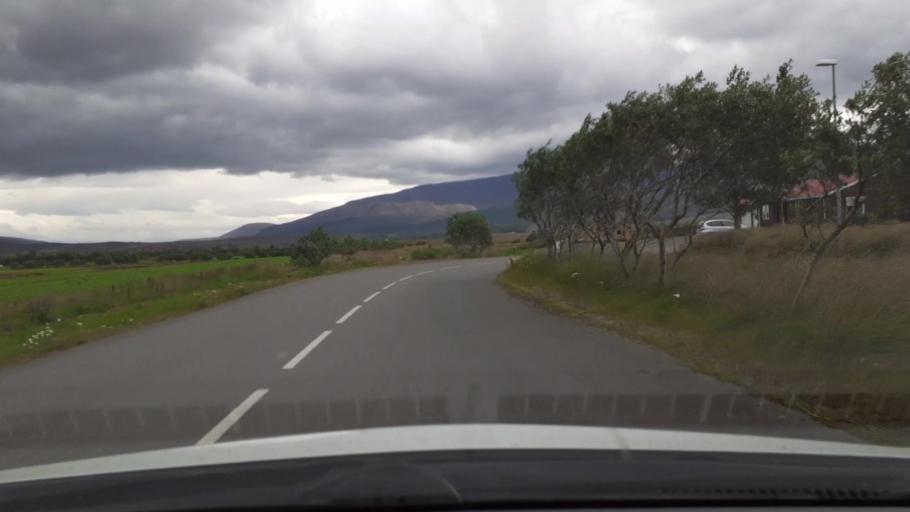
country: IS
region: West
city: Borgarnes
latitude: 64.5617
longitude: -21.7559
